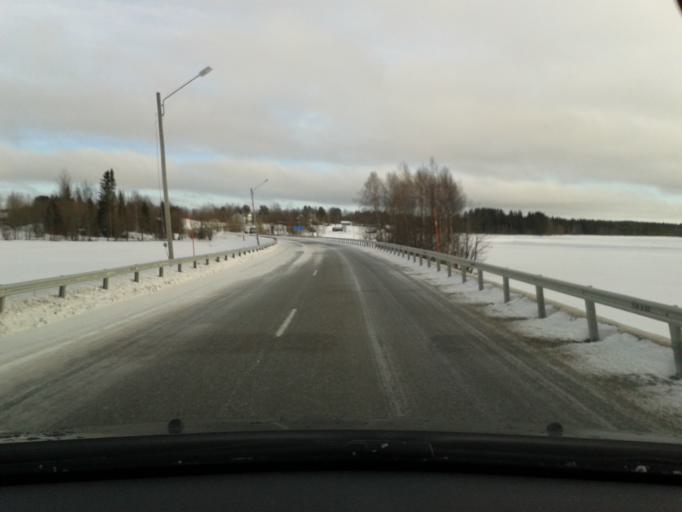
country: SE
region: Vaesterbotten
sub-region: Vilhelmina Kommun
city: Sjoberg
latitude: 64.6320
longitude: 16.3908
